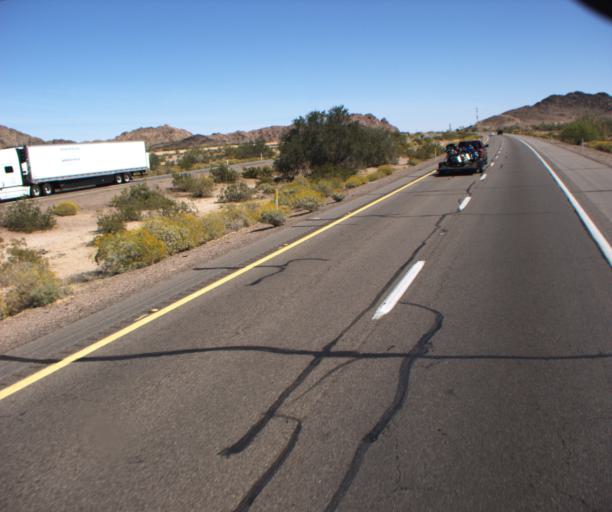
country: US
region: Arizona
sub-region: Yuma County
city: Wellton
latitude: 32.7222
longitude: -113.7631
